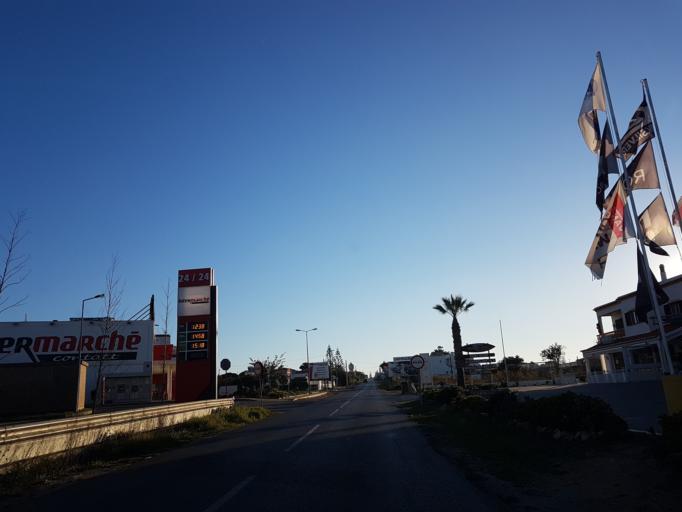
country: PT
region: Faro
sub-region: Vila do Bispo
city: Sagres
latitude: 37.0155
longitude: -8.9412
